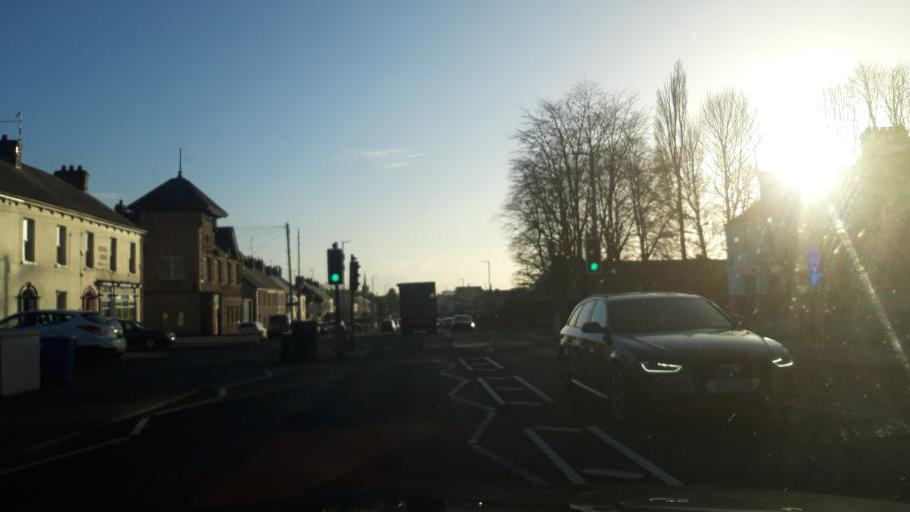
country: GB
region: Northern Ireland
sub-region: Cookstown District
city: Cookstown
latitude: 54.6430
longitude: -6.7446
